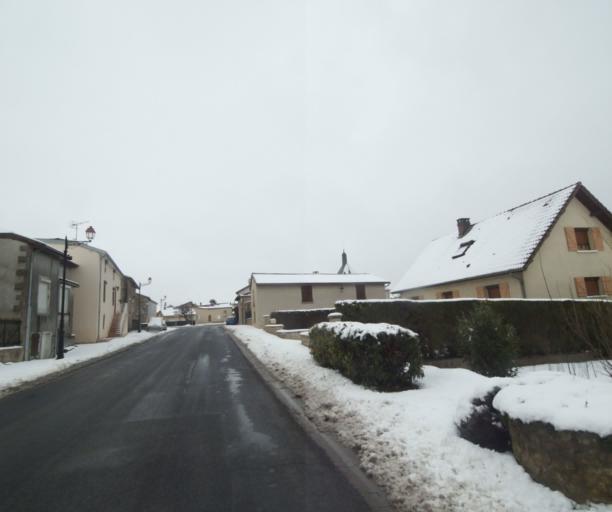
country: FR
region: Champagne-Ardenne
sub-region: Departement de la Haute-Marne
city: Wassy
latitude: 48.4286
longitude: 4.9634
